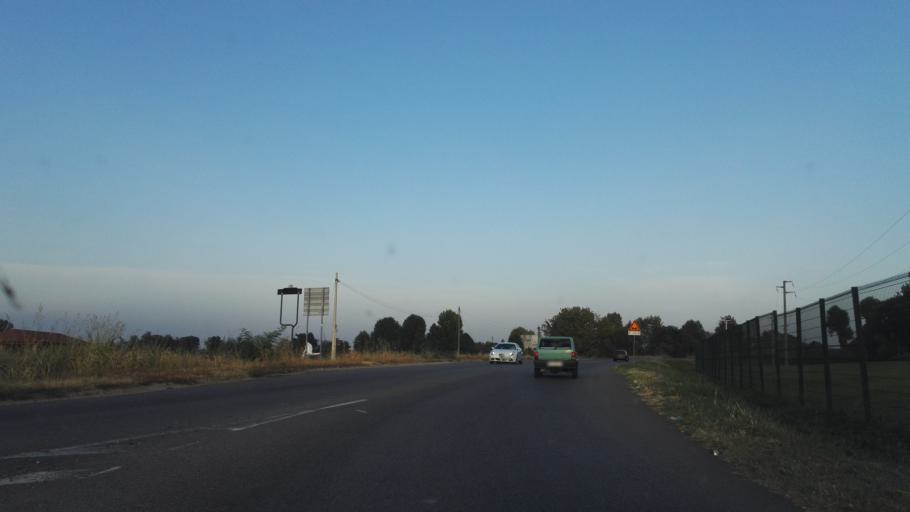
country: IT
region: Lombardy
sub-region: Citta metropolitana di Milano
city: Paullo
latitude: 45.4273
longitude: 9.3952
